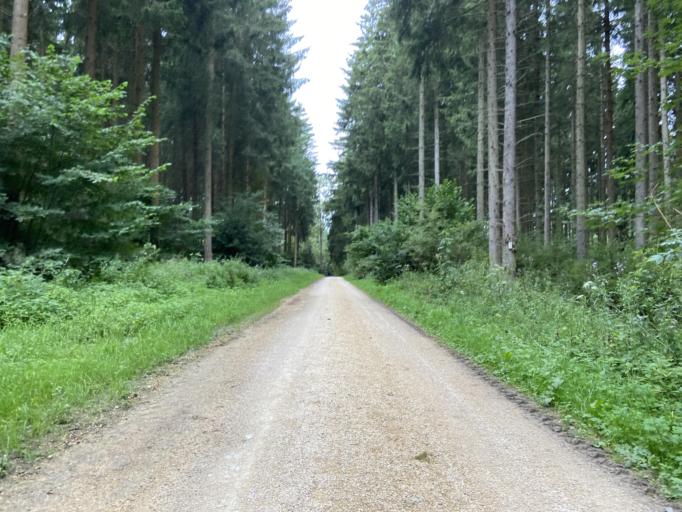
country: DE
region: Baden-Wuerttemberg
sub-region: Tuebingen Region
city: Sigmaringendorf
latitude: 48.0843
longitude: 9.2614
